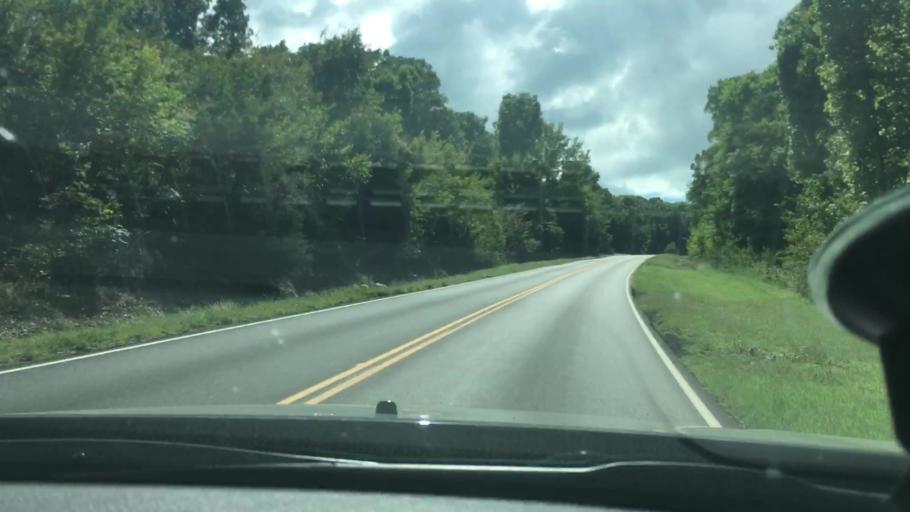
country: US
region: Oklahoma
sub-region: Sequoyah County
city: Vian
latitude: 35.6671
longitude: -94.9374
